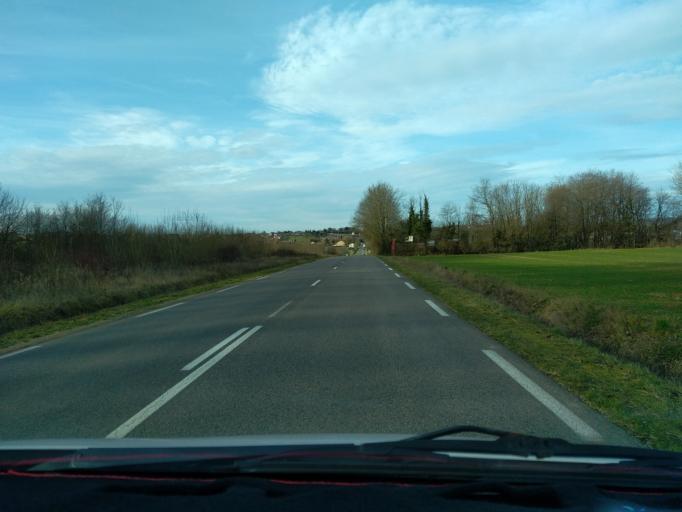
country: FR
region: Franche-Comte
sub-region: Departement de la Haute-Saone
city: Gray
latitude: 47.4276
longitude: 5.6096
